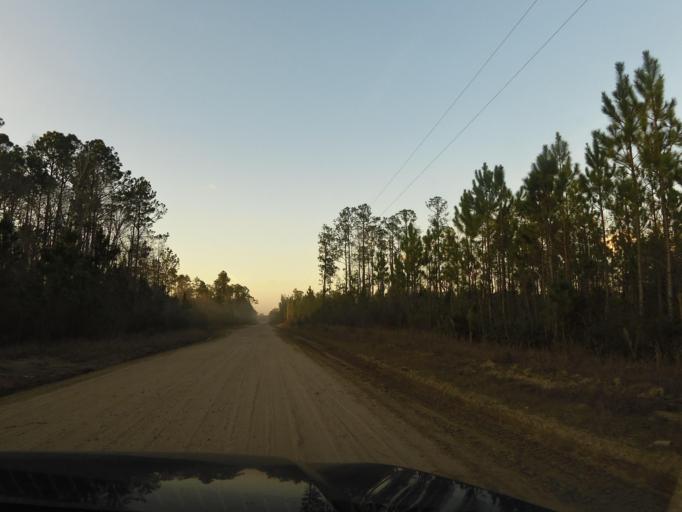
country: US
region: Florida
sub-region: Clay County
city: Green Cove Springs
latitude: 29.8578
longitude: -81.7968
